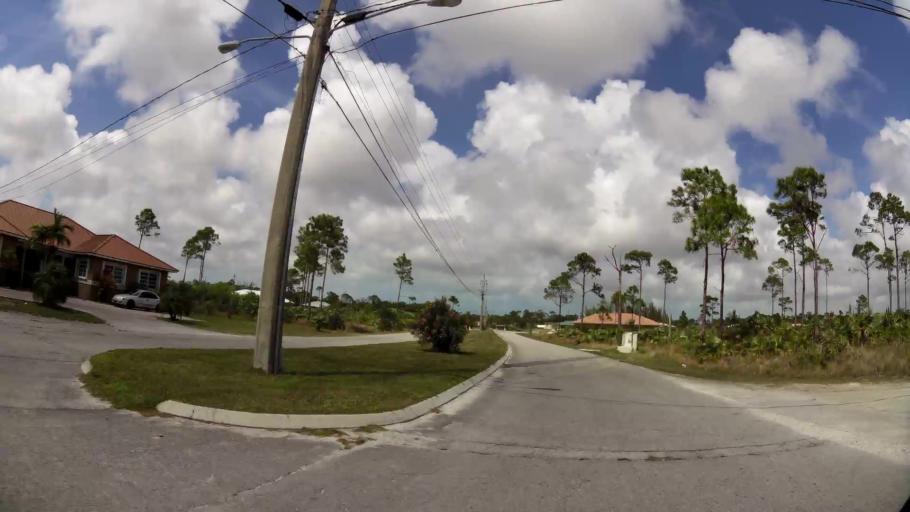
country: BS
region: Freeport
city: Freeport
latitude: 26.5148
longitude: -78.7222
